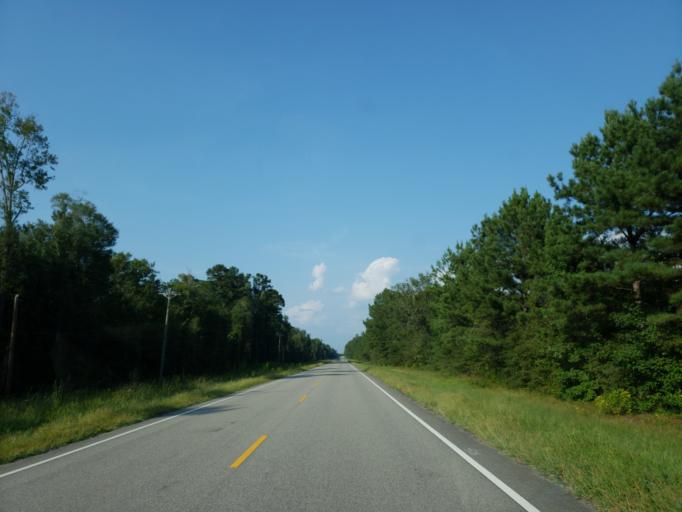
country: US
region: Alabama
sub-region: Sumter County
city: Livingston
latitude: 32.7316
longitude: -88.0598
